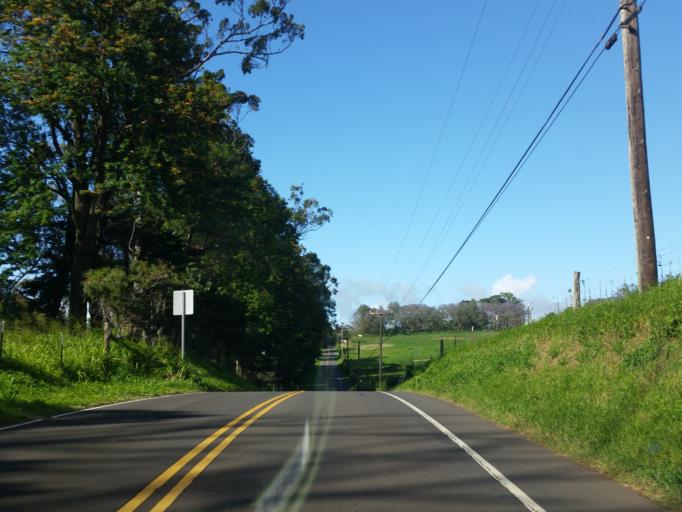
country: US
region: Hawaii
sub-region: Maui County
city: Pukalani
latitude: 20.8321
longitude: -156.3143
